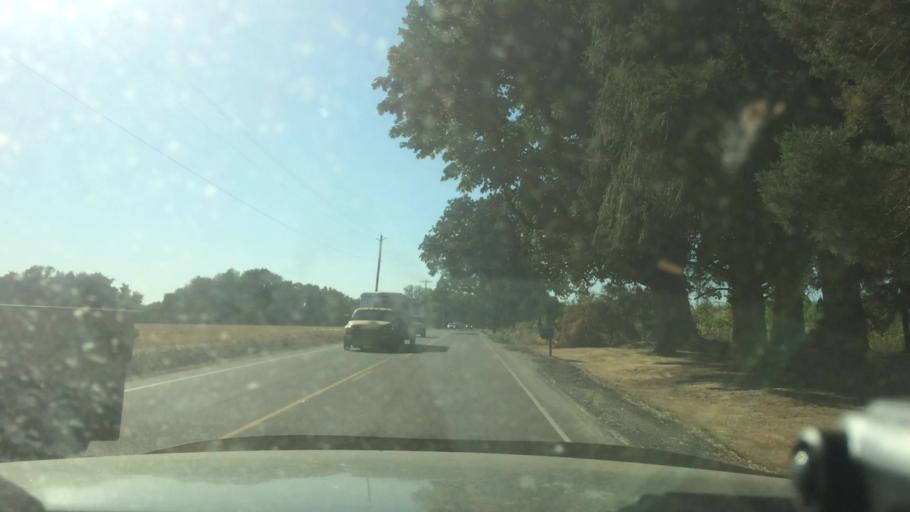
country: US
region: Oregon
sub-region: Marion County
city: Gervais
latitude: 45.1286
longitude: -122.9971
